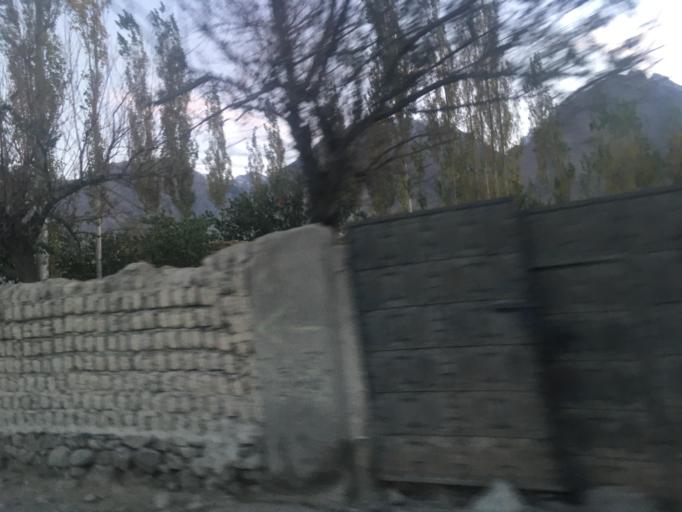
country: PK
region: Gilgit-Baltistan
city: Skardu
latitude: 35.3005
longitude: 75.5433
